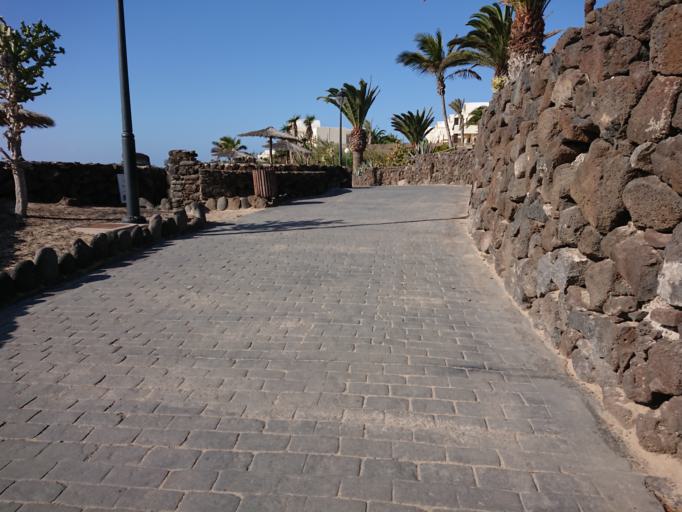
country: ES
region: Canary Islands
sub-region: Provincia de Las Palmas
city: Playa Blanca
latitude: 28.8615
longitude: -13.8609
